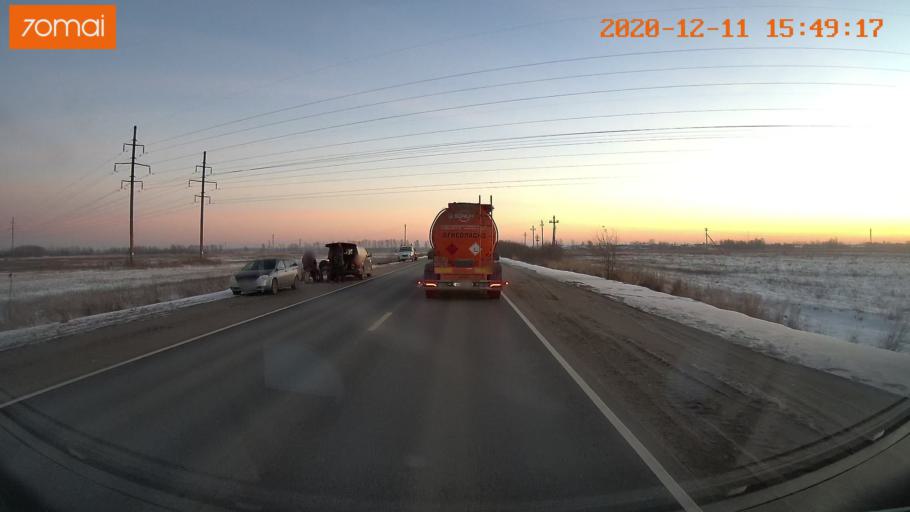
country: RU
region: Ivanovo
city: Novo-Talitsy
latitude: 56.9889
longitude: 40.8734
